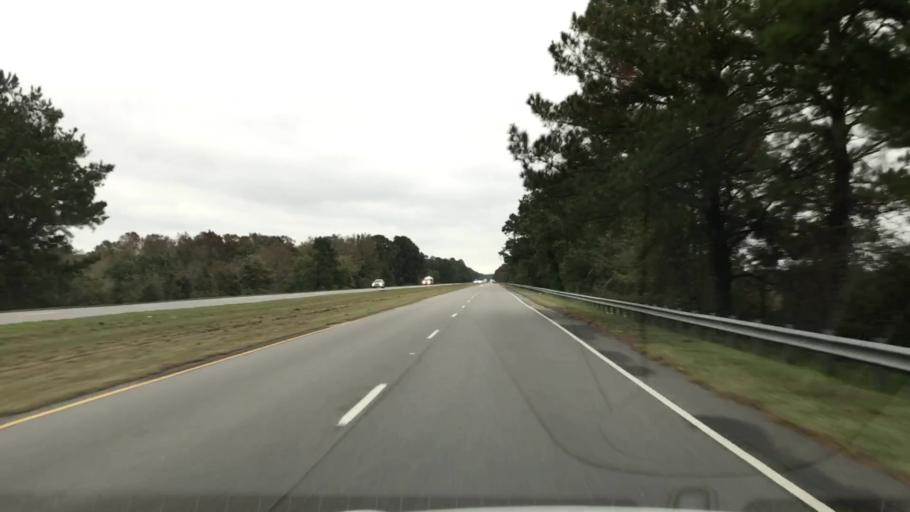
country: US
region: South Carolina
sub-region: Georgetown County
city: Georgetown
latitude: 33.1908
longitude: -79.3999
